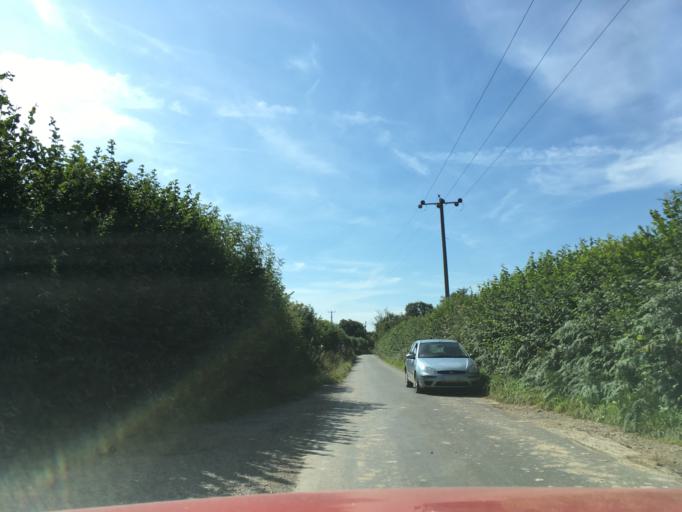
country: GB
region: England
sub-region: Hampshire
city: Highclere
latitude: 51.3130
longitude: -1.3845
